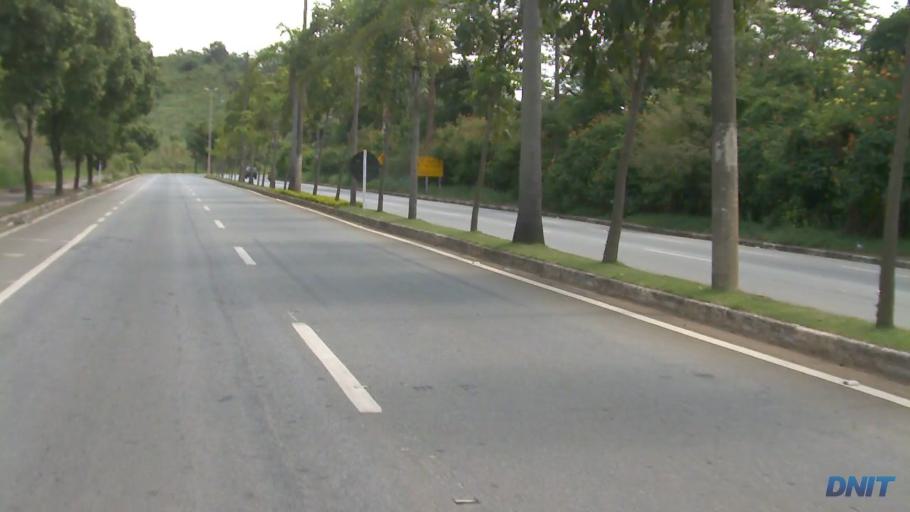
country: BR
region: Minas Gerais
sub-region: Coronel Fabriciano
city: Coronel Fabriciano
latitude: -19.5083
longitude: -42.5822
